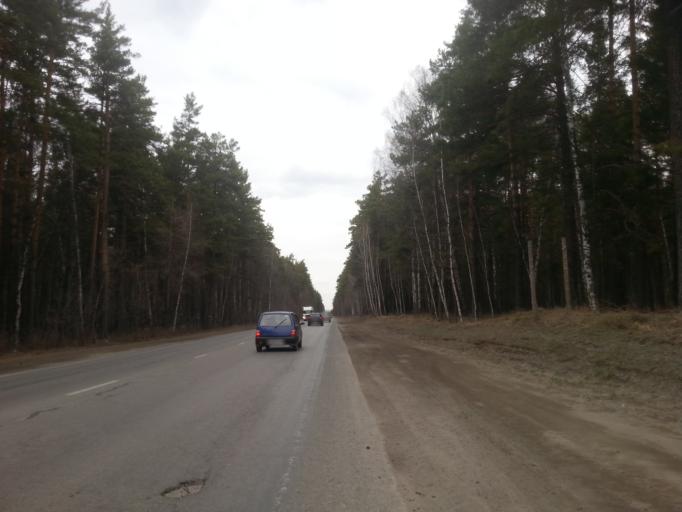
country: RU
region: Altai Krai
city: Yuzhnyy
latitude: 53.2776
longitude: 83.7192
